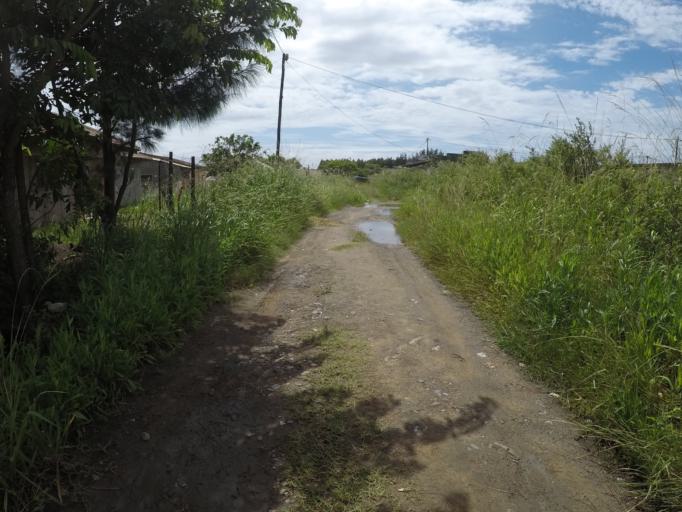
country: ZA
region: KwaZulu-Natal
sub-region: uThungulu District Municipality
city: eSikhawini
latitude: -28.8571
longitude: 31.9287
